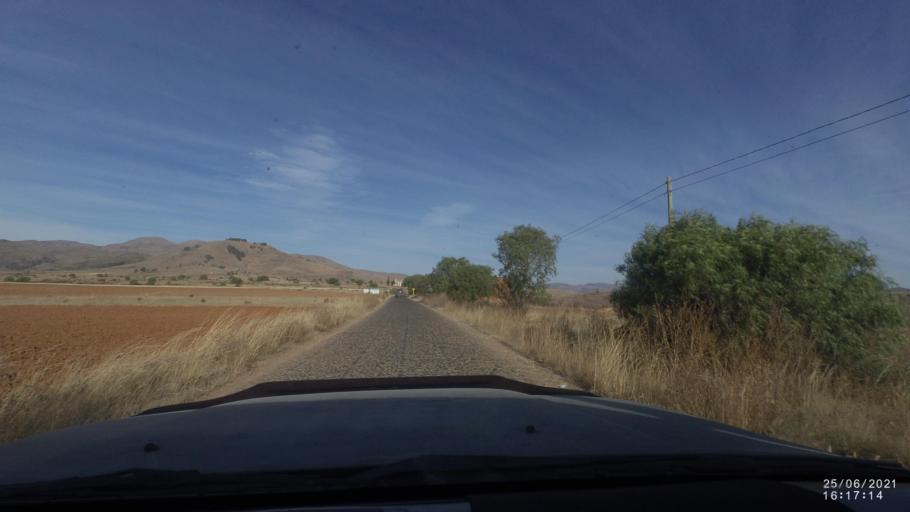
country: BO
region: Cochabamba
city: Cliza
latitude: -17.7253
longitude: -65.8582
